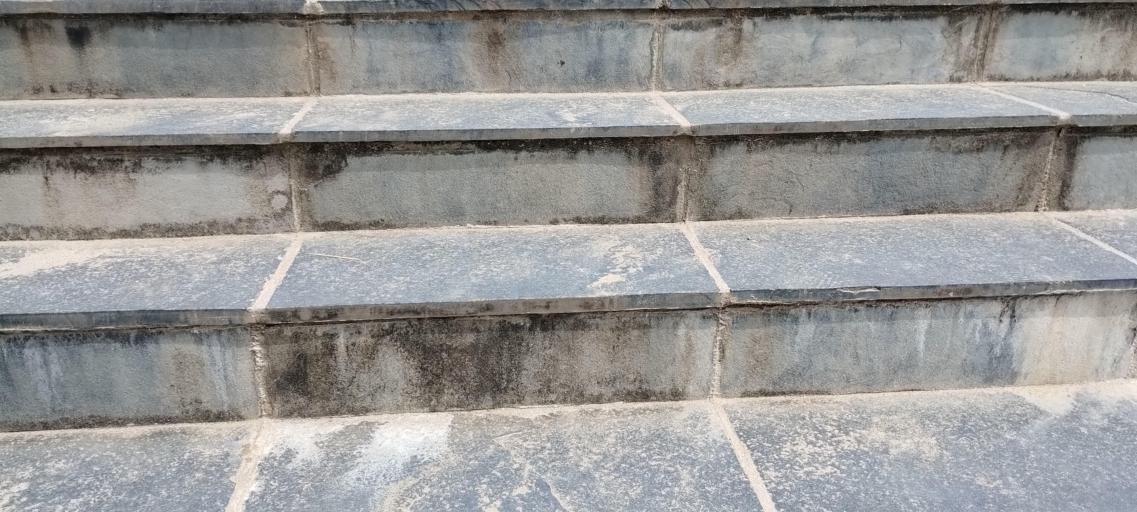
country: NP
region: Central Region
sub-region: Bagmati Zone
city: Kathmandu
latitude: 27.7903
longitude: 85.3609
